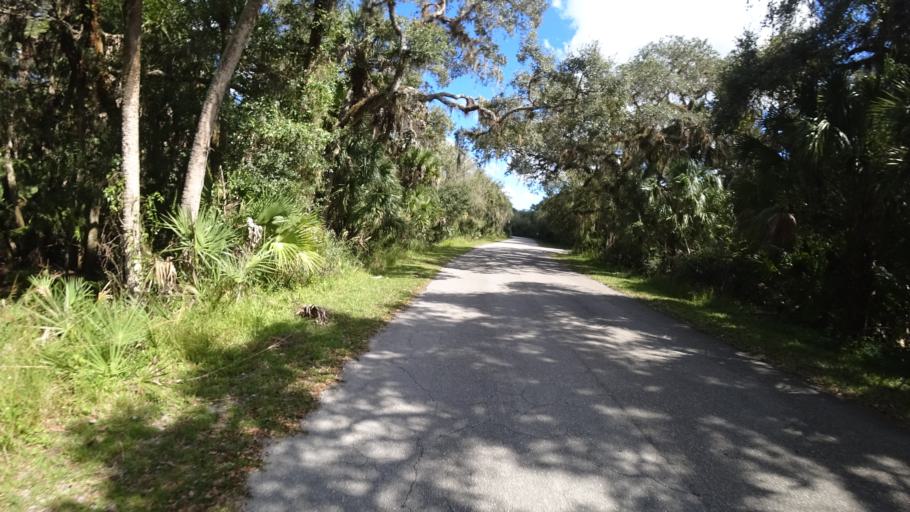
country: US
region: Florida
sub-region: Sarasota County
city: Lake Sarasota
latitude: 27.2861
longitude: -82.2554
